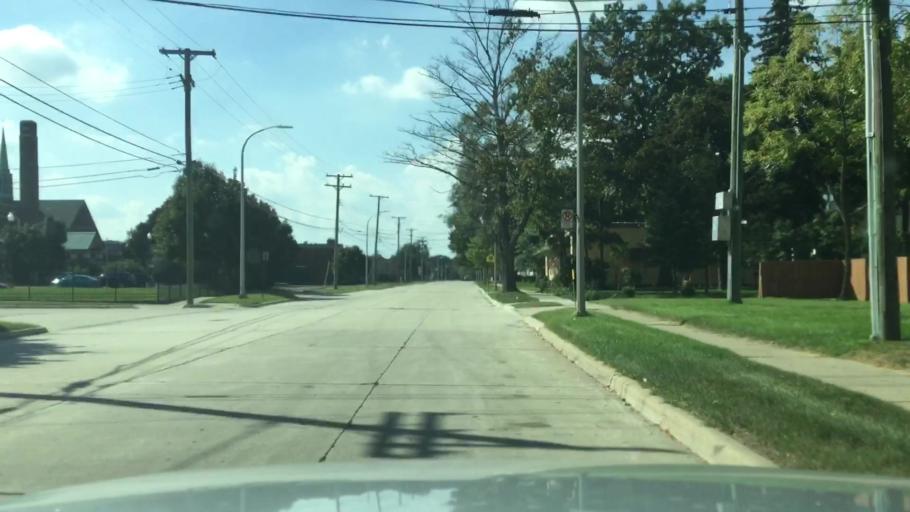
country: US
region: Michigan
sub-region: Wayne County
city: Wayne
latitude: 42.2823
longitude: -83.3774
